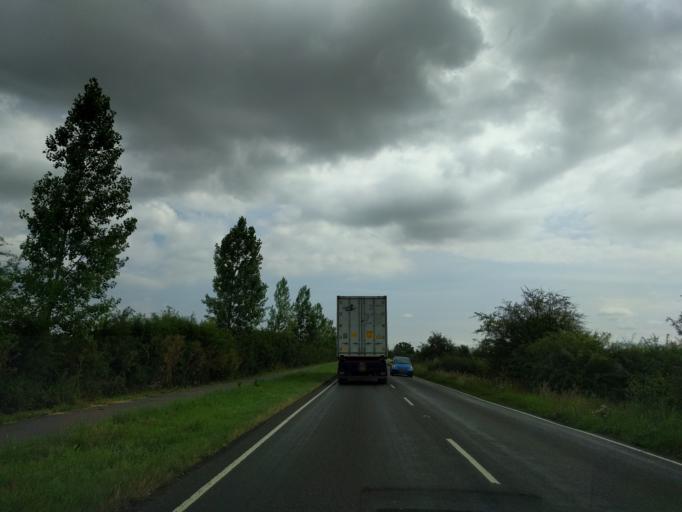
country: GB
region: England
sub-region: Cambridgeshire
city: Needingworth
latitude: 52.3419
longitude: -0.0118
